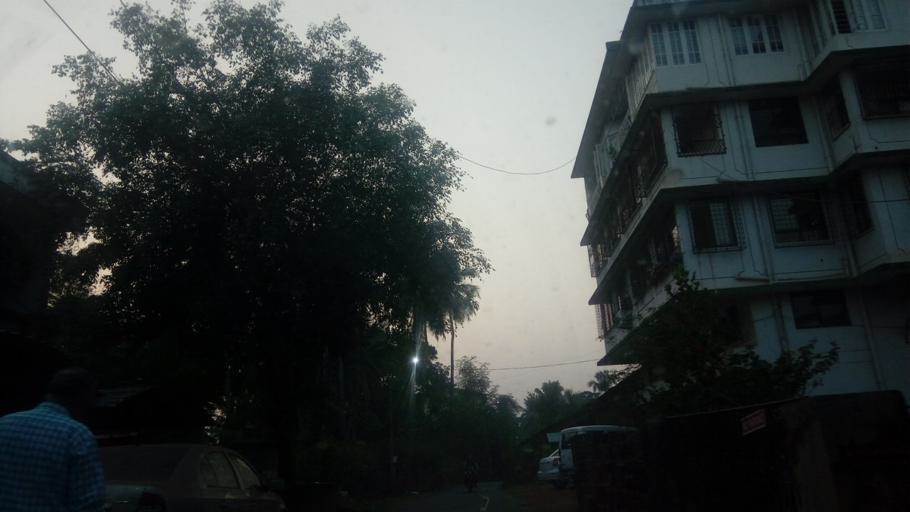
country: IN
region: Goa
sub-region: South Goa
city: Madgaon
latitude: 15.2885
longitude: 73.9609
